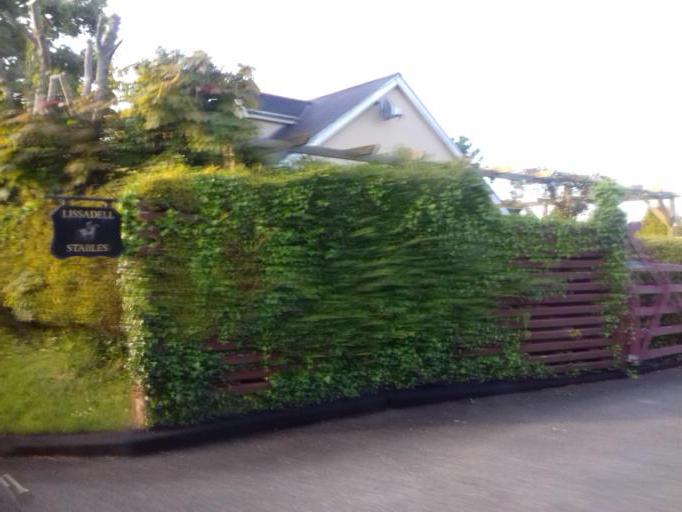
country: IE
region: Leinster
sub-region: Fingal County
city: Swords
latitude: 53.4819
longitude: -6.2249
